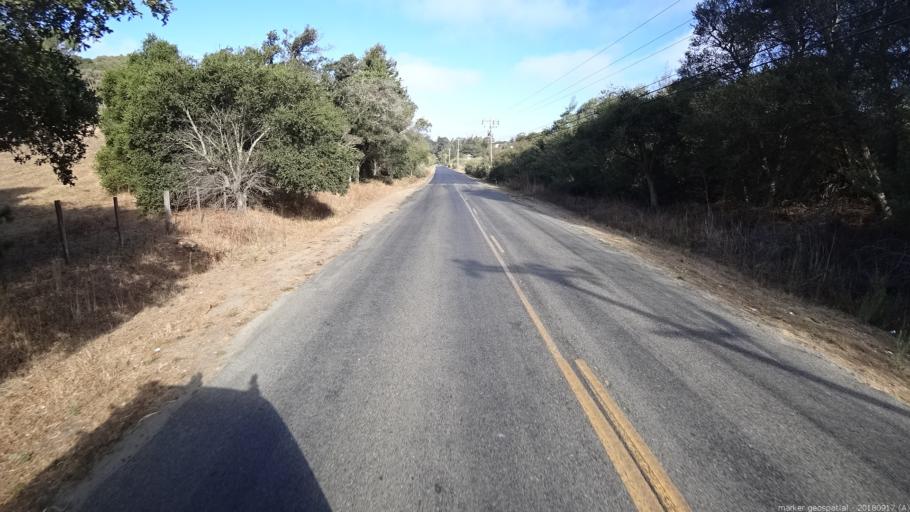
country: US
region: California
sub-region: Monterey County
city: Prunedale
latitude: 36.7995
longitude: -121.6988
